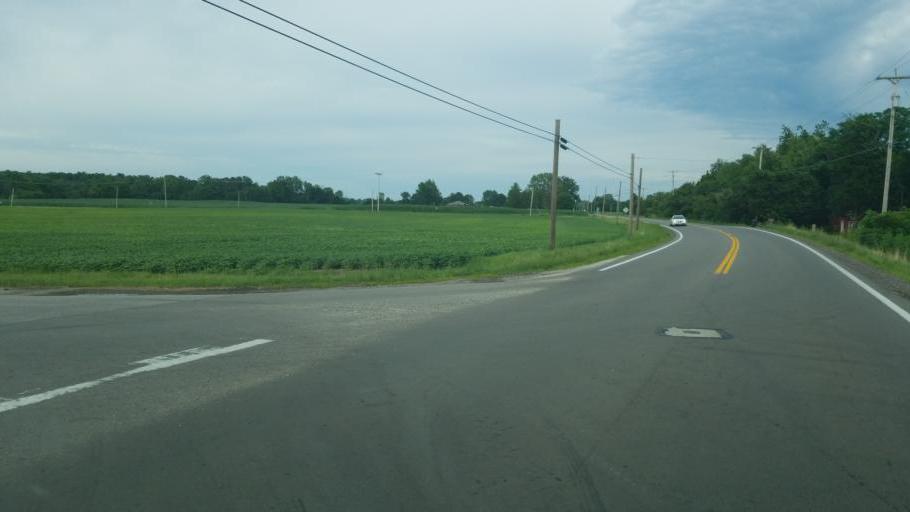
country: US
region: Ohio
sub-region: Morrow County
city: Cardington
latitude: 40.5166
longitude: -82.8644
